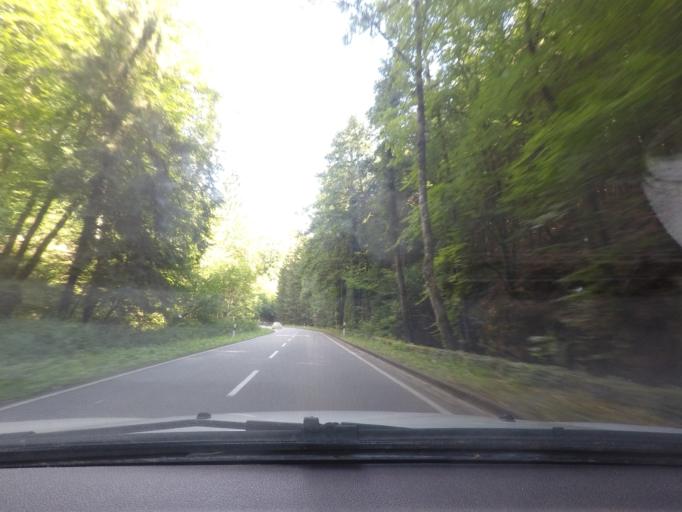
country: LU
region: Luxembourg
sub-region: Canton de Mersch
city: Heffingen
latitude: 49.7532
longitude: 6.2717
